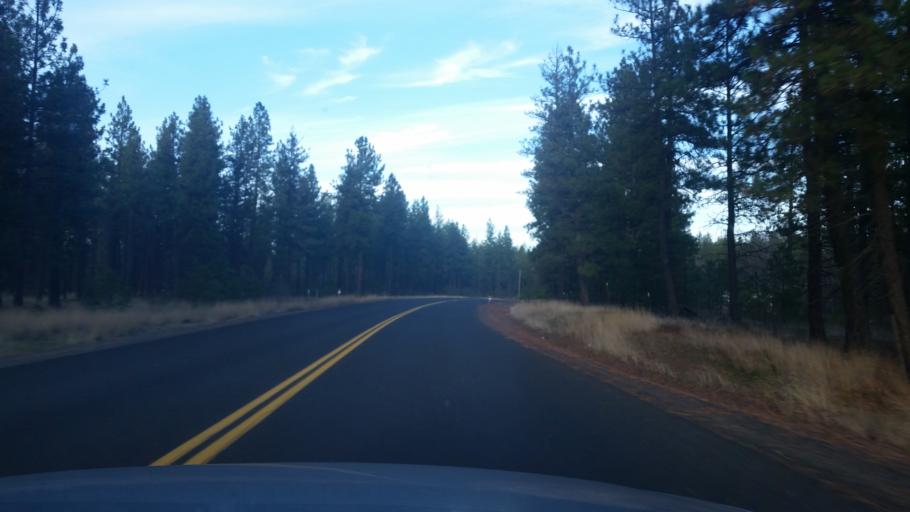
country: US
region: Washington
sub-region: Spokane County
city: Cheney
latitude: 47.4751
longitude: -117.5401
